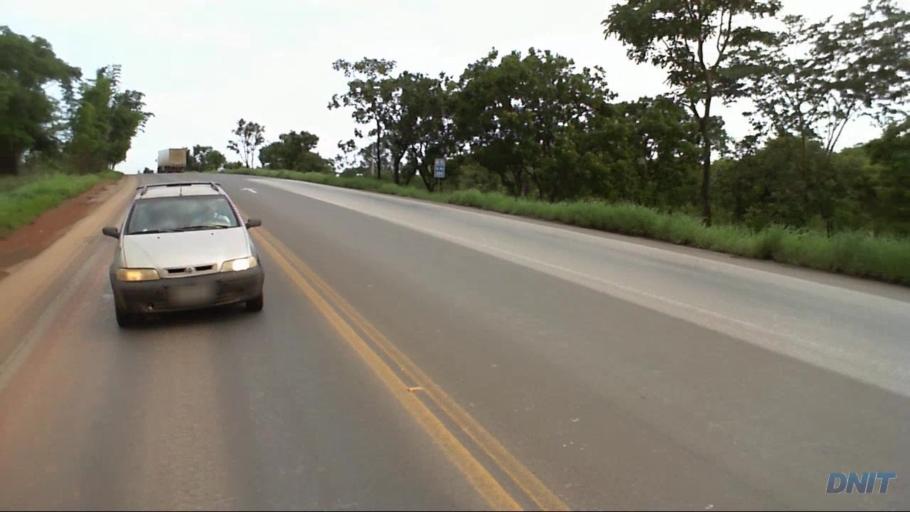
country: BR
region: Goias
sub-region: Uruacu
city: Uruacu
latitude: -14.5647
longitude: -49.1563
